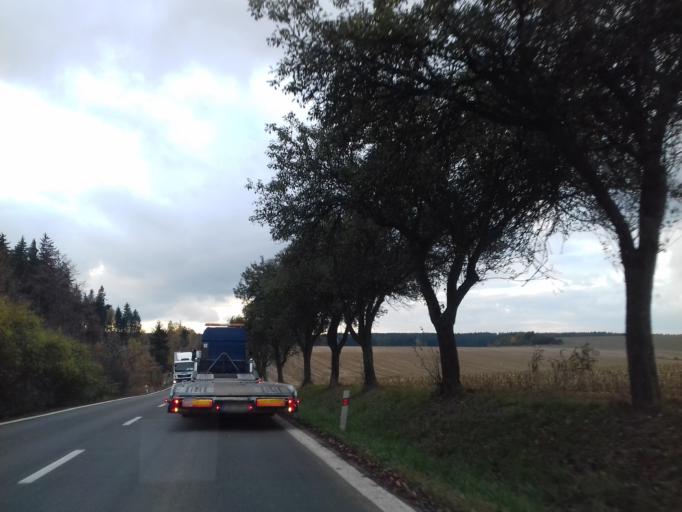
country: CZ
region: Pardubicky
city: Pomezi
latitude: 49.7321
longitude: 16.3405
